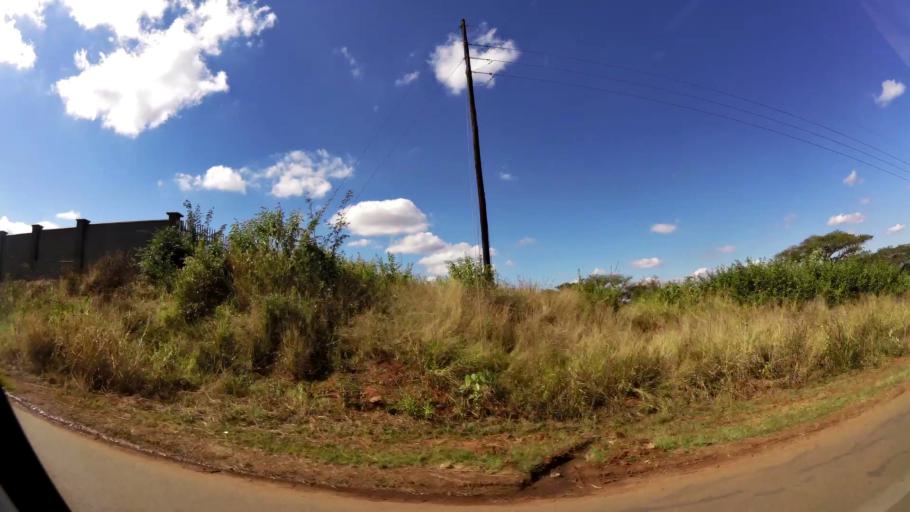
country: ZA
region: Limpopo
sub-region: Mopani District Municipality
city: Tzaneen
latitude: -23.8117
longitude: 30.1598
